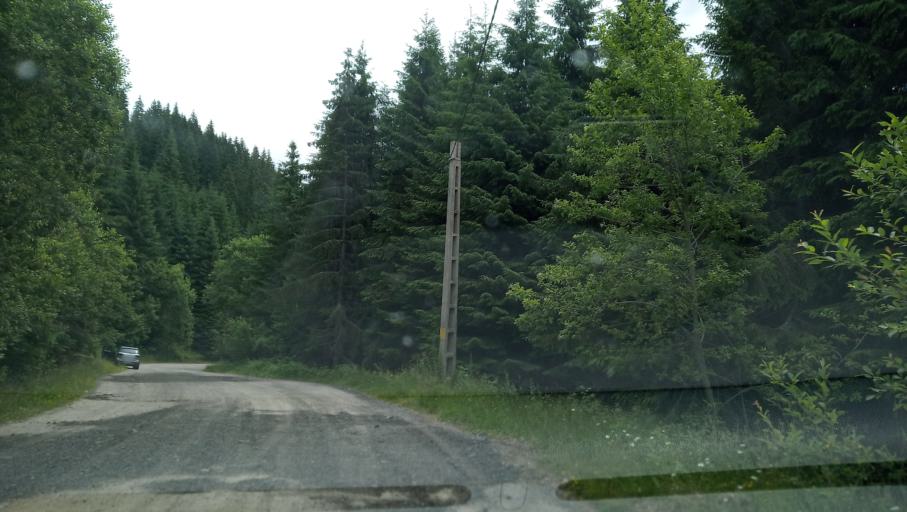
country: RO
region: Valcea
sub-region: Comuna Voineasa
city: Voineasa
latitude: 45.4252
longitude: 23.7611
